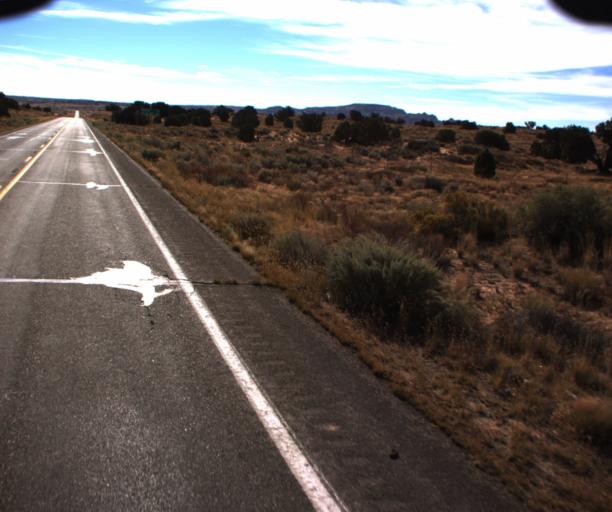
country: US
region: Arizona
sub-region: Coconino County
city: Kaibito
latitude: 36.5958
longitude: -111.1644
